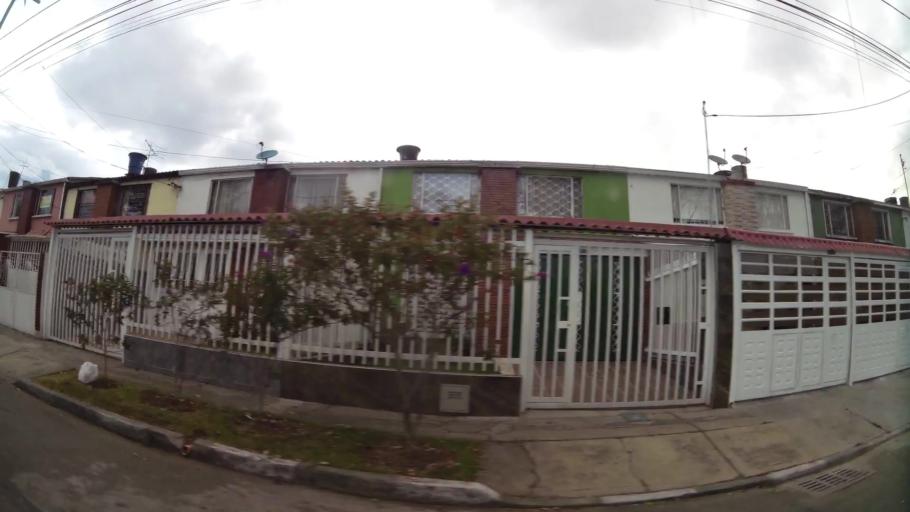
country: CO
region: Bogota D.C.
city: Bogota
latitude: 4.5961
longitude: -74.1255
